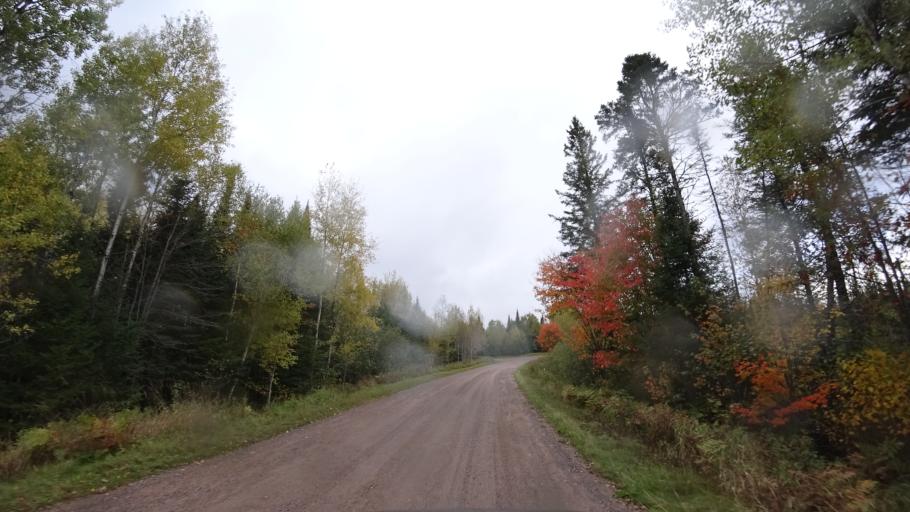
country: US
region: Wisconsin
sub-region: Sawyer County
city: Little Round Lake
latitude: 45.9866
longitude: -90.9997
